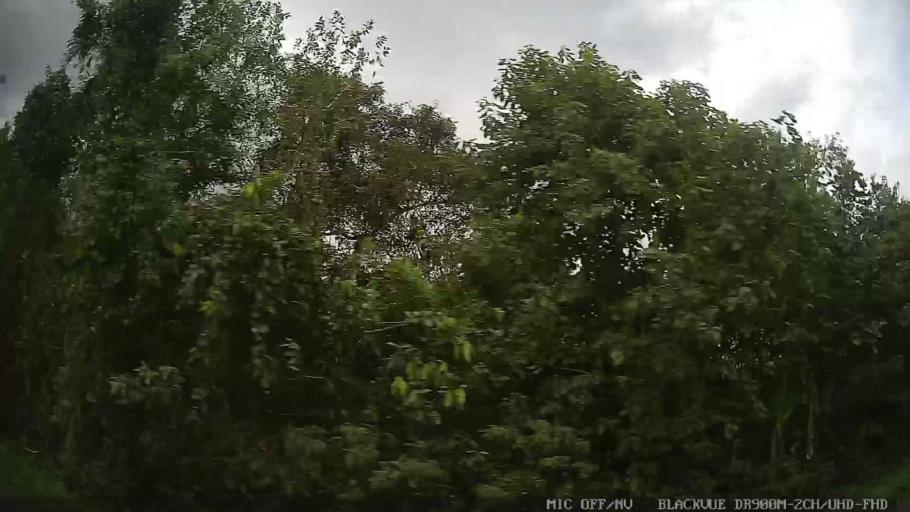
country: BR
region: Sao Paulo
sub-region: Cubatao
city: Cubatao
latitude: -23.8589
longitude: -46.3518
